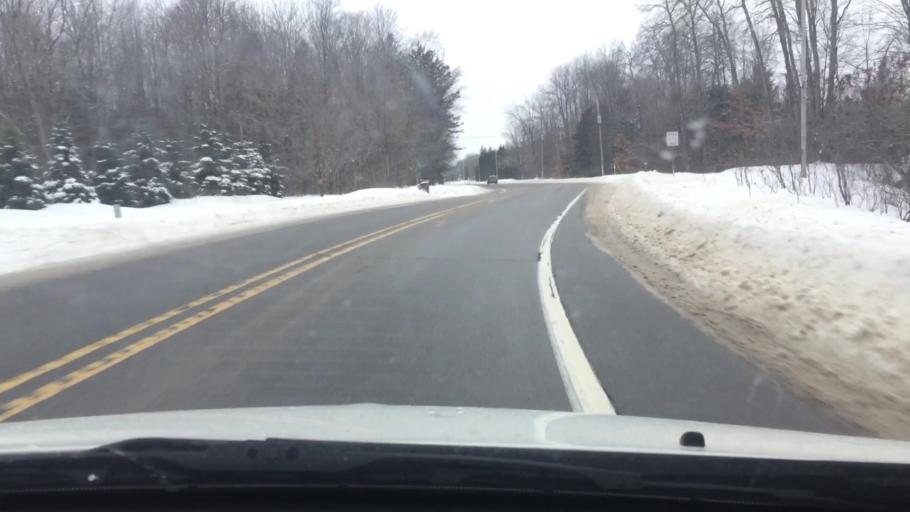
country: US
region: Michigan
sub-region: Charlevoix County
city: East Jordan
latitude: 45.1324
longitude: -85.0935
